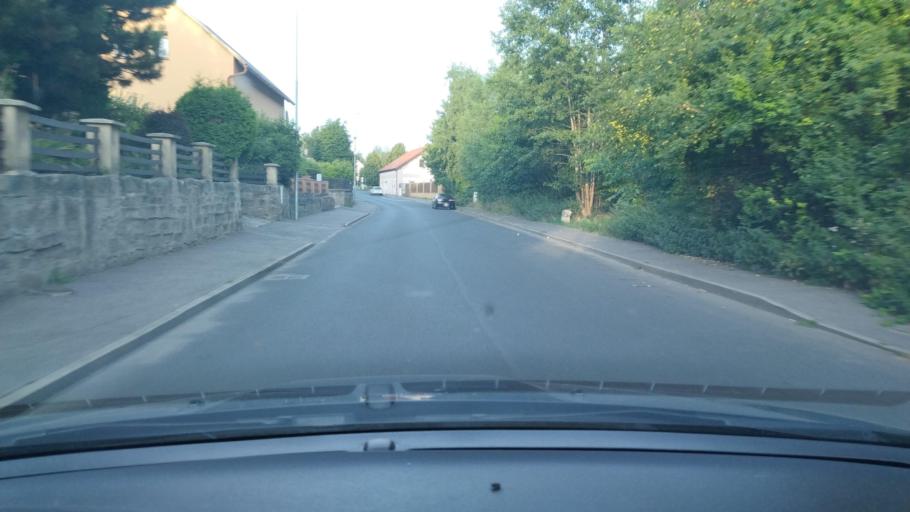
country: CZ
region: Liberecky
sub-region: Okres Ceska Lipa
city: Ceska Lipa
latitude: 50.6840
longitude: 14.5513
